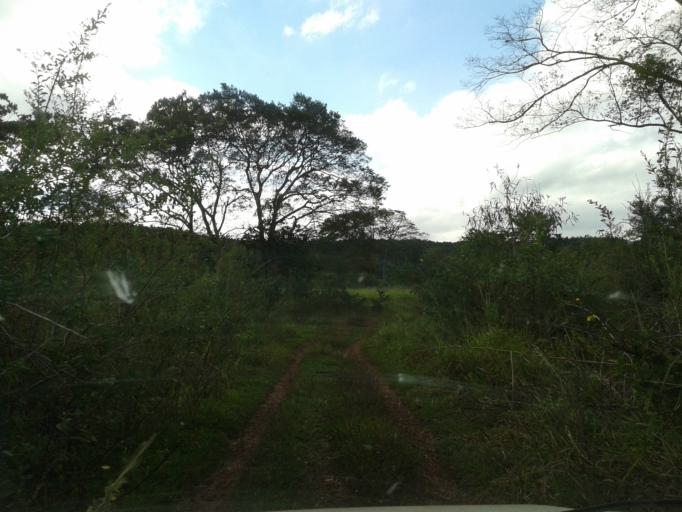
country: BR
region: Minas Gerais
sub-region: Campina Verde
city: Campina Verde
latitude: -19.4632
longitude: -49.6329
